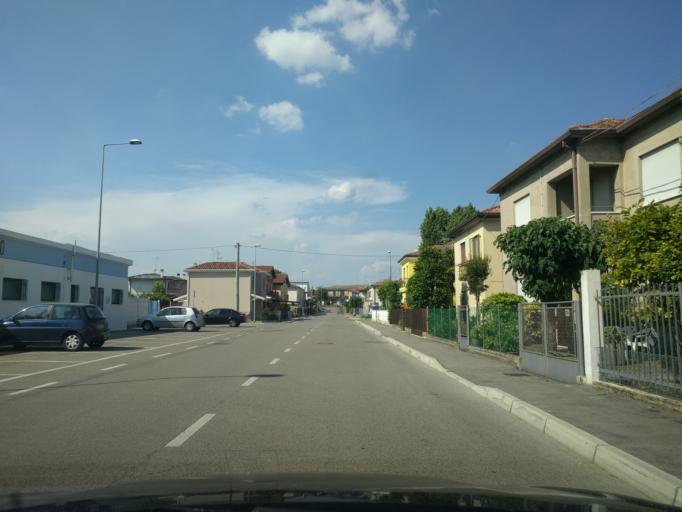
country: IT
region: Veneto
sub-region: Provincia di Rovigo
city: Villadose
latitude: 45.0726
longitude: 11.8875
